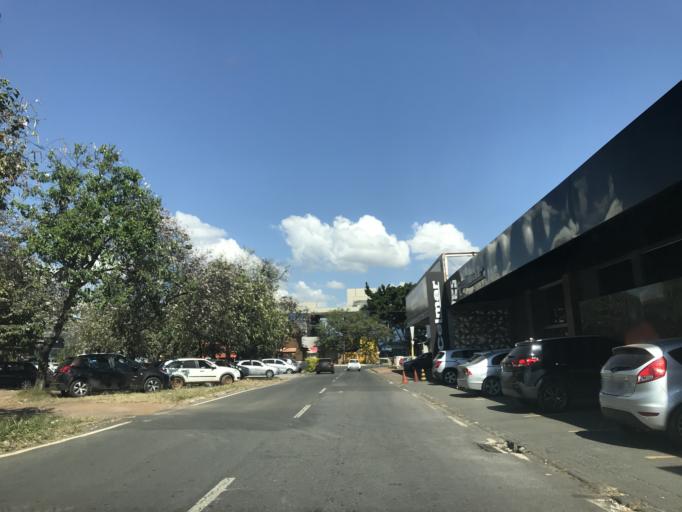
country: BR
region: Federal District
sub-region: Brasilia
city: Brasilia
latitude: -15.8051
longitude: -47.9585
